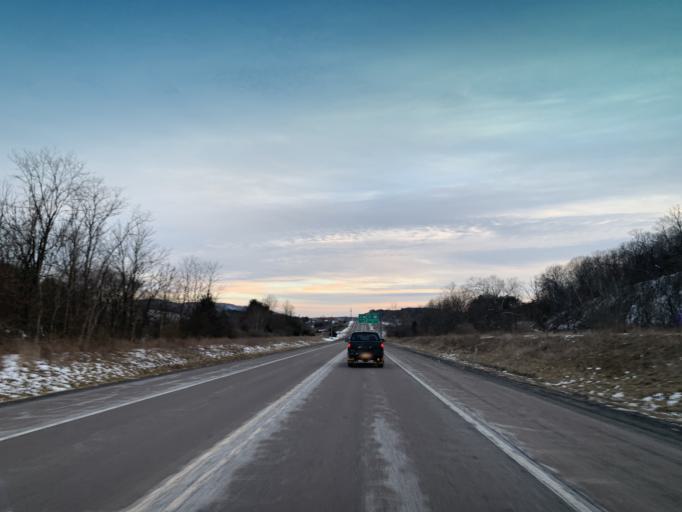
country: US
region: Maryland
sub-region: Allegany County
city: Cumberland
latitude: 39.6813
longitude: -78.7156
